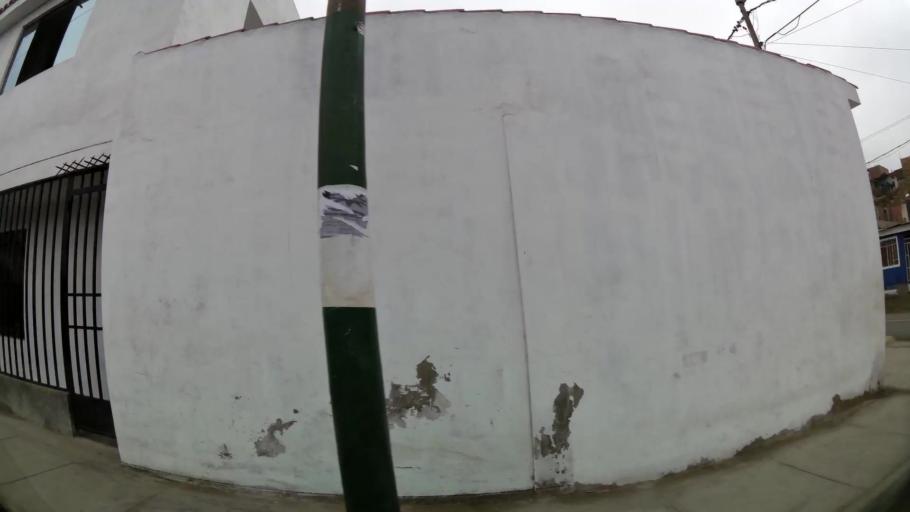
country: PE
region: Lima
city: Ventanilla
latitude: -11.8786
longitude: -77.1347
